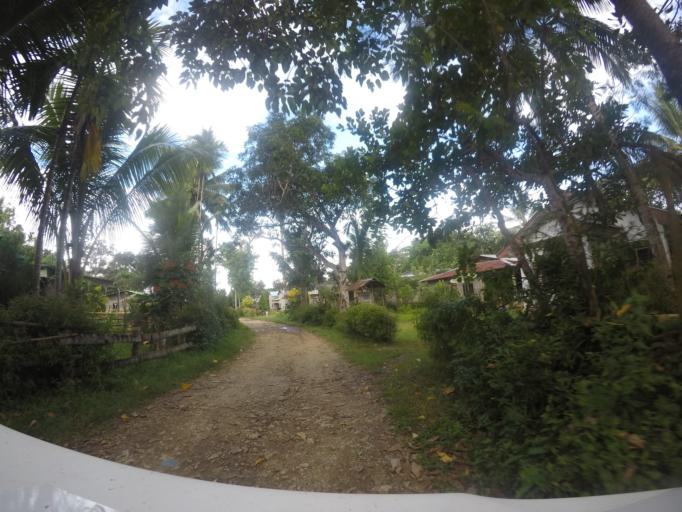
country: TL
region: Lautem
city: Lospalos
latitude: -8.5031
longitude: 126.9928
